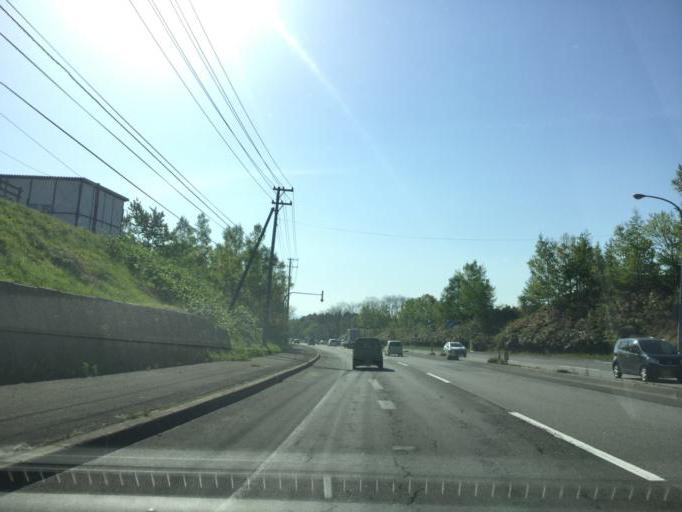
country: JP
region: Hokkaido
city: Kitahiroshima
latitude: 42.9998
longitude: 141.5365
